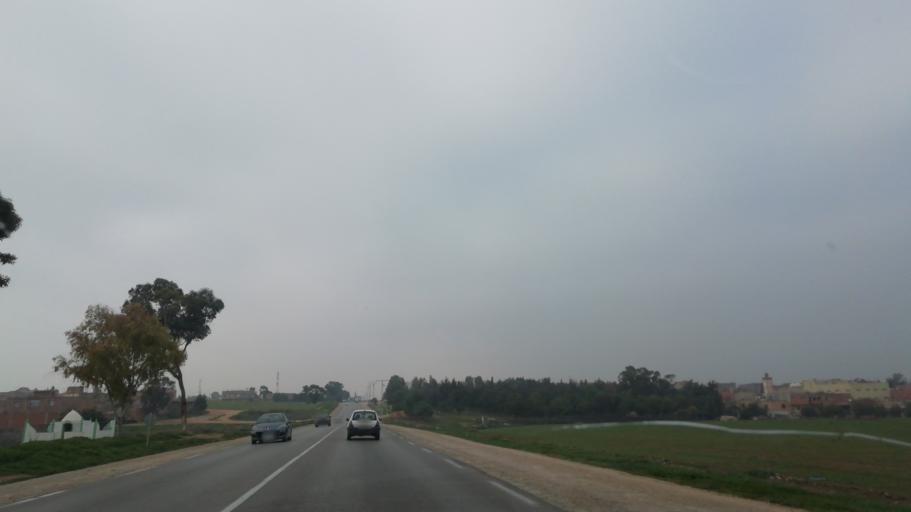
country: DZ
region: Relizane
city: Djidiouia
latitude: 35.8944
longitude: 0.7436
